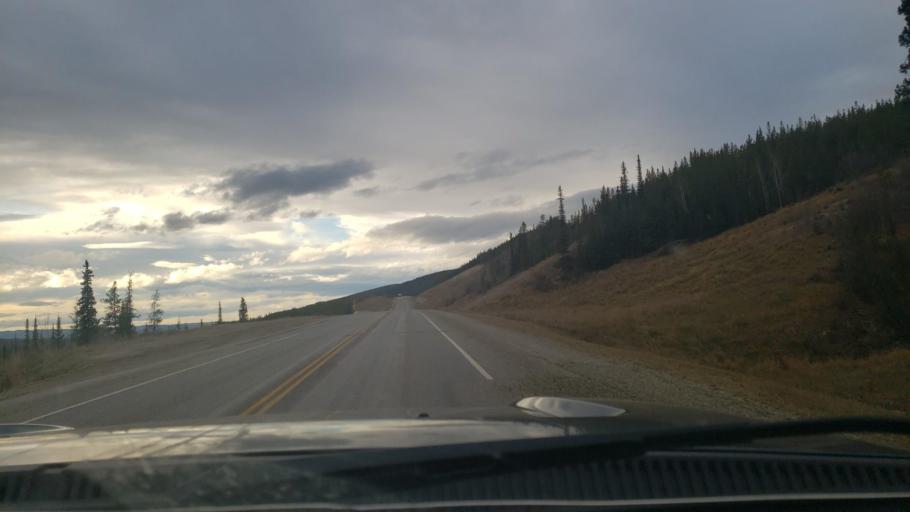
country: CA
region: Yukon
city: Watson Lake
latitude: 59.7497
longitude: -127.3612
